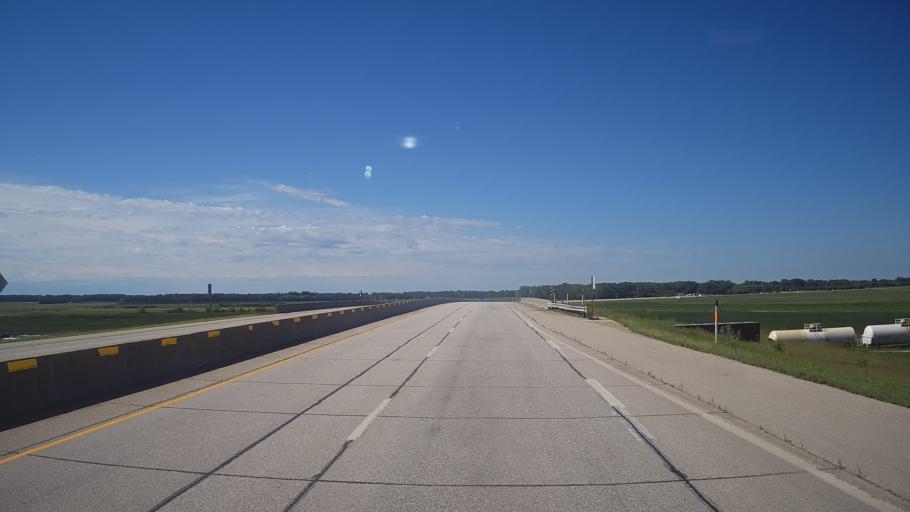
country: CA
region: Manitoba
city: Portage la Prairie
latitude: 49.9688
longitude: -98.2339
